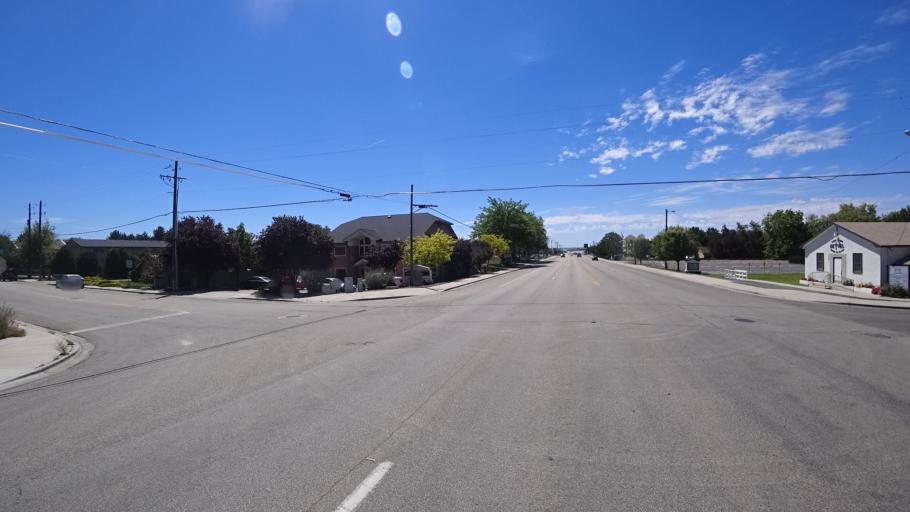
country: US
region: Idaho
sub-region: Ada County
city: Garden City
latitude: 43.5827
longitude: -116.2436
